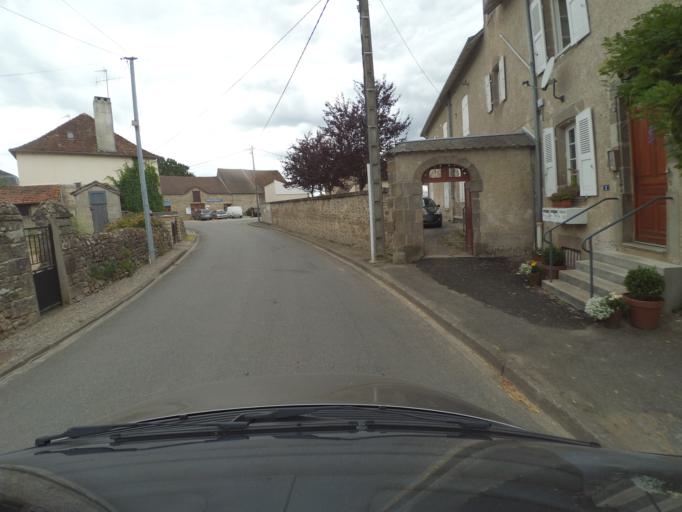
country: FR
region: Limousin
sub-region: Departement de la Haute-Vienne
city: Magnac-Laval
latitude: 46.2872
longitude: 1.2471
